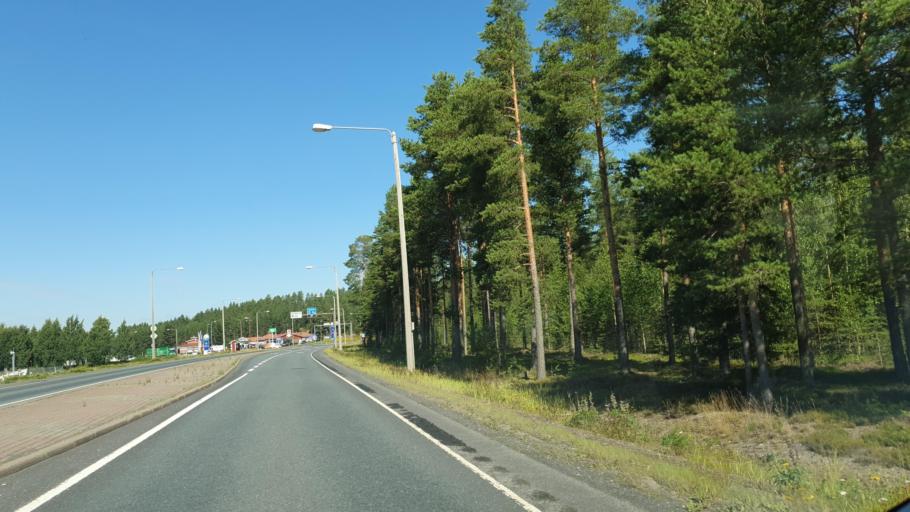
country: FI
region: Northern Savo
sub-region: Ylae-Savo
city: Lapinlahti
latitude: 63.3457
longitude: 27.4162
